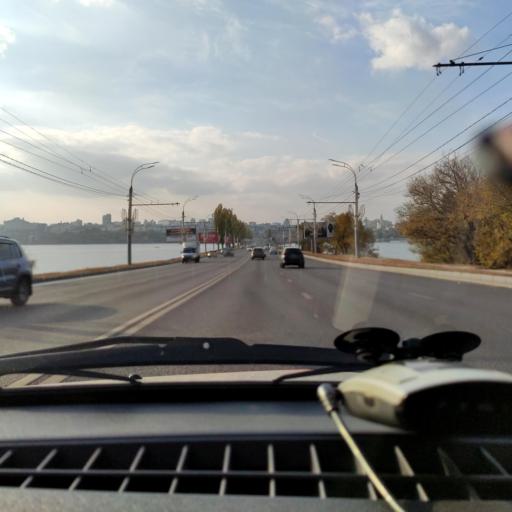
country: RU
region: Voronezj
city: Voronezh
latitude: 51.6654
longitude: 39.2424
